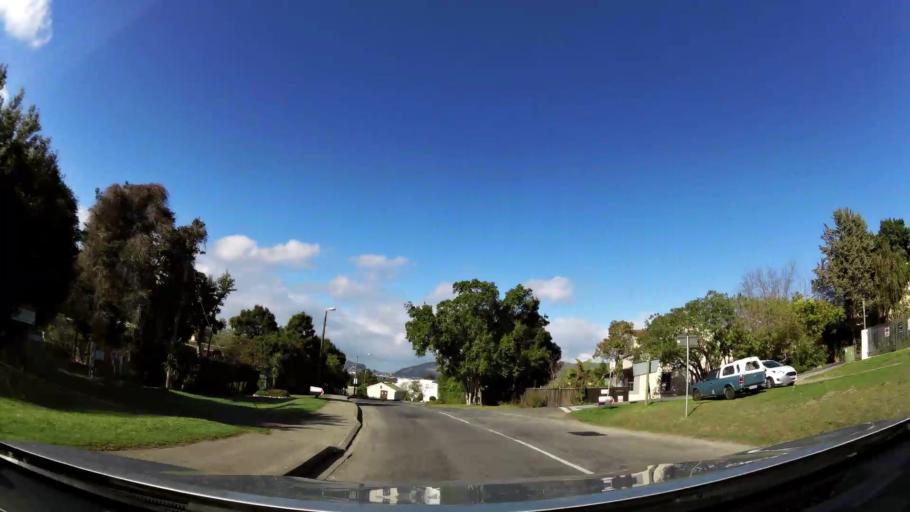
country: ZA
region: Western Cape
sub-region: Eden District Municipality
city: Knysna
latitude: -34.0325
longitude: 23.0469
